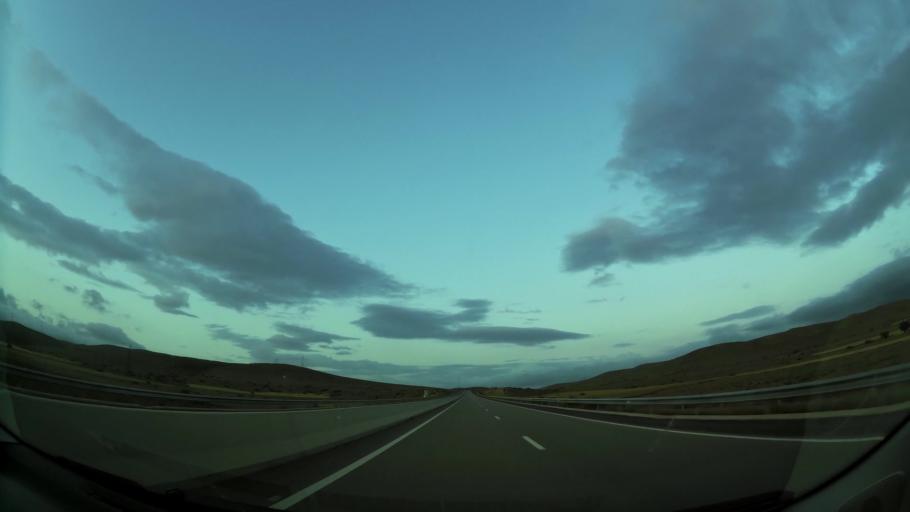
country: MA
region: Oriental
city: El Aioun
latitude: 34.6054
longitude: -2.6004
